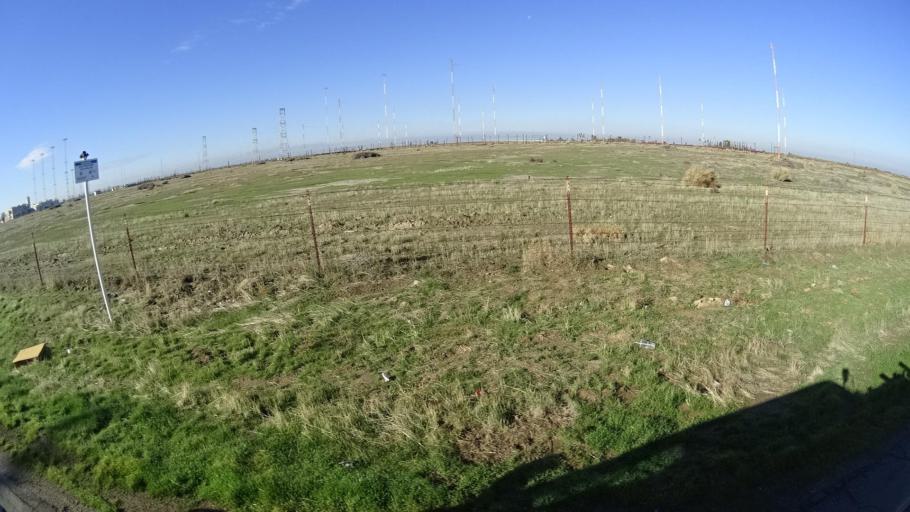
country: US
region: California
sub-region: Kern County
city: Delano
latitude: 35.7586
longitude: -119.2763
